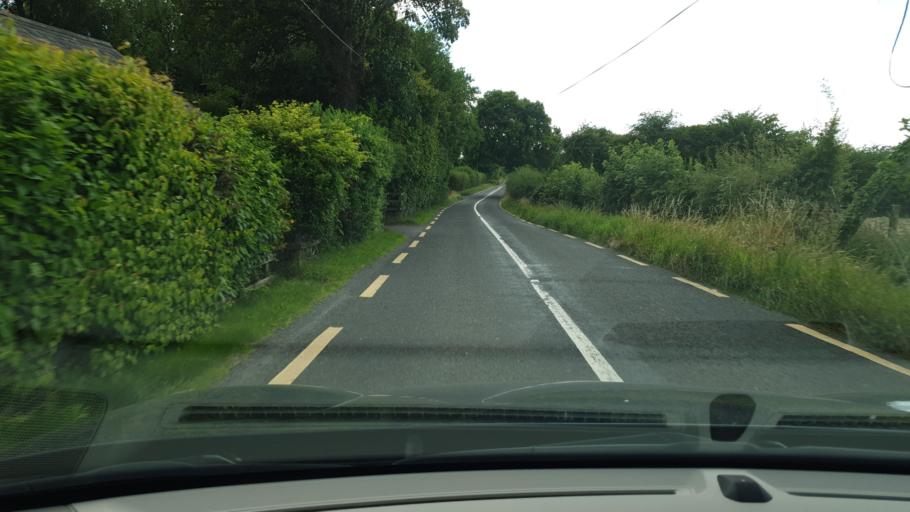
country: IE
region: Leinster
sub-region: Kildare
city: Kilcock
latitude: 53.4646
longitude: -6.6287
